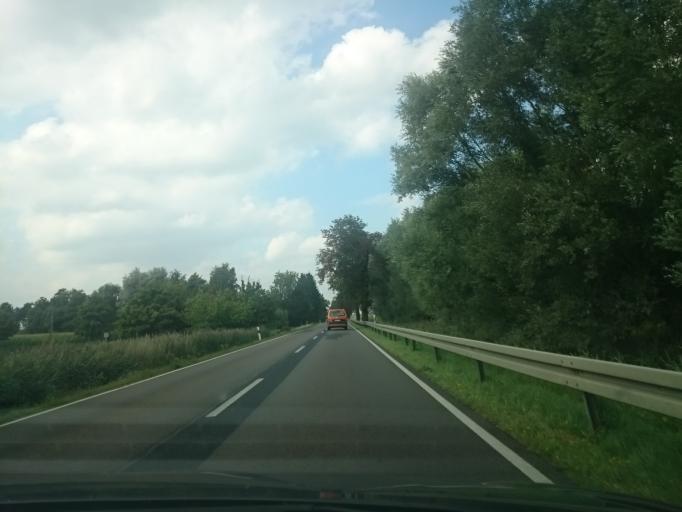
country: DE
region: Mecklenburg-Vorpommern
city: Ferdinandshof
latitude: 53.6473
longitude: 13.9115
